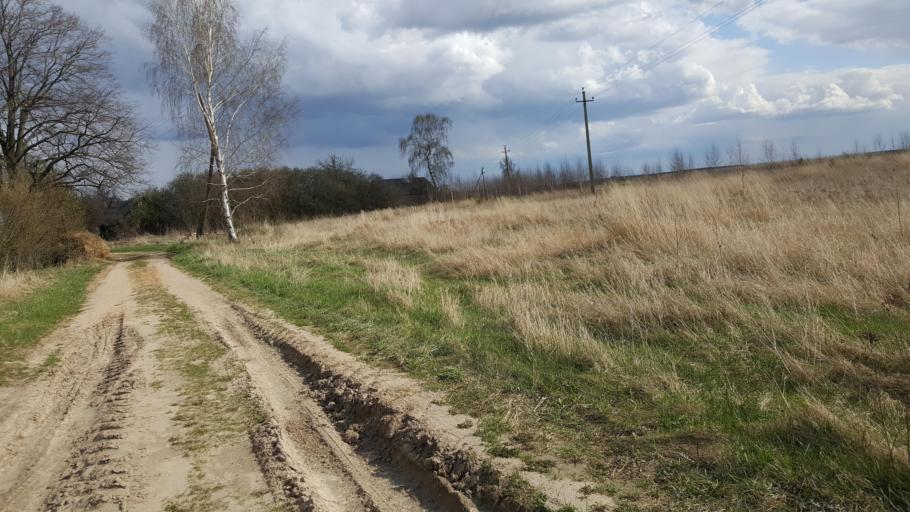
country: BY
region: Brest
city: Kamyanyets
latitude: 52.4378
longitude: 23.6799
